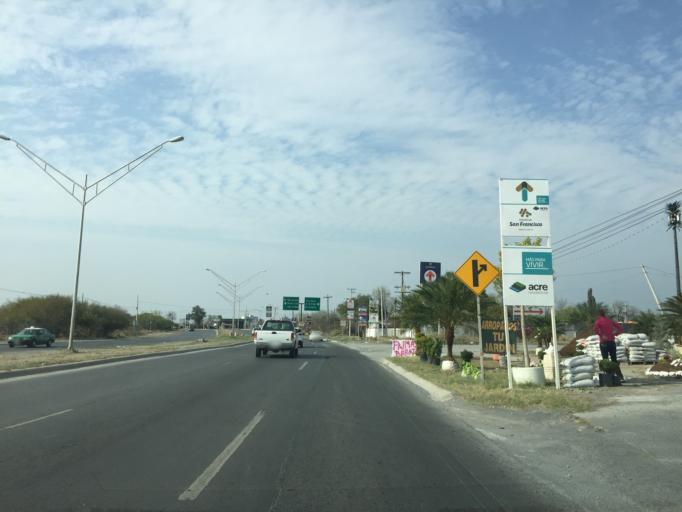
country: MX
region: Nuevo Leon
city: Apodaca
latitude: 25.7706
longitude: -100.1995
